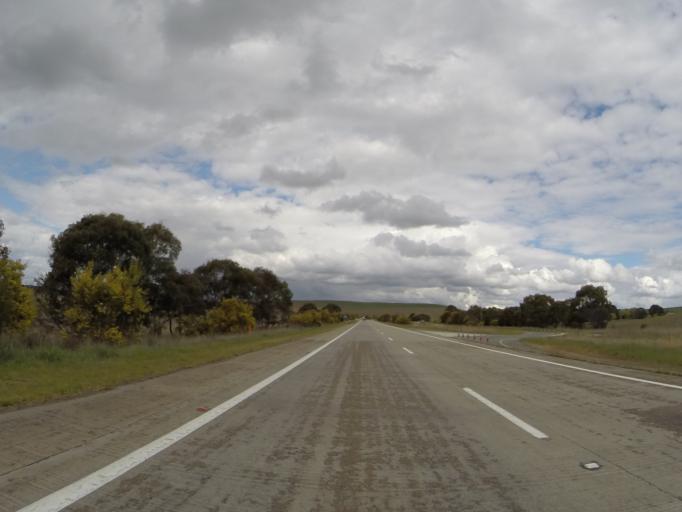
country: AU
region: New South Wales
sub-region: Goulburn Mulwaree
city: Goulburn
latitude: -34.8049
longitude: 149.5135
